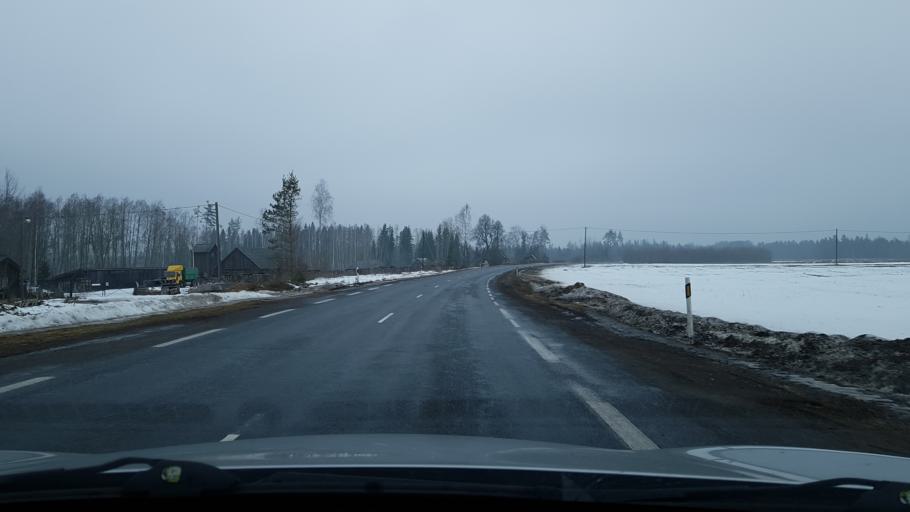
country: EE
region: Valgamaa
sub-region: Torva linn
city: Torva
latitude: 58.1593
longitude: 25.9622
